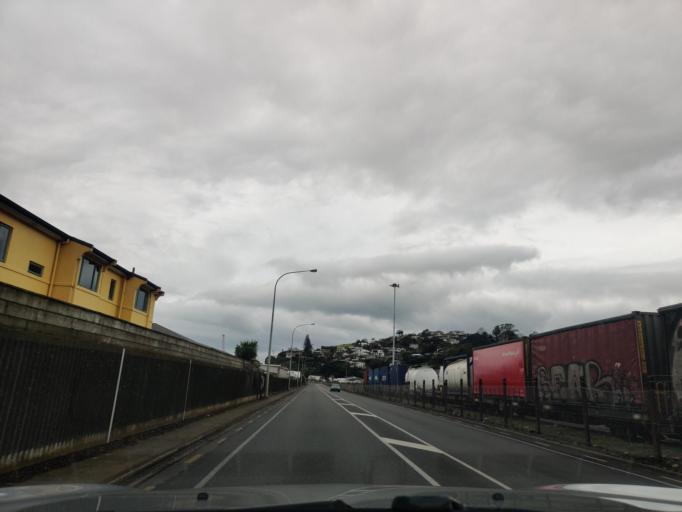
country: NZ
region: Hawke's Bay
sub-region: Napier City
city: Napier
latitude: -39.4801
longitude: 176.9025
